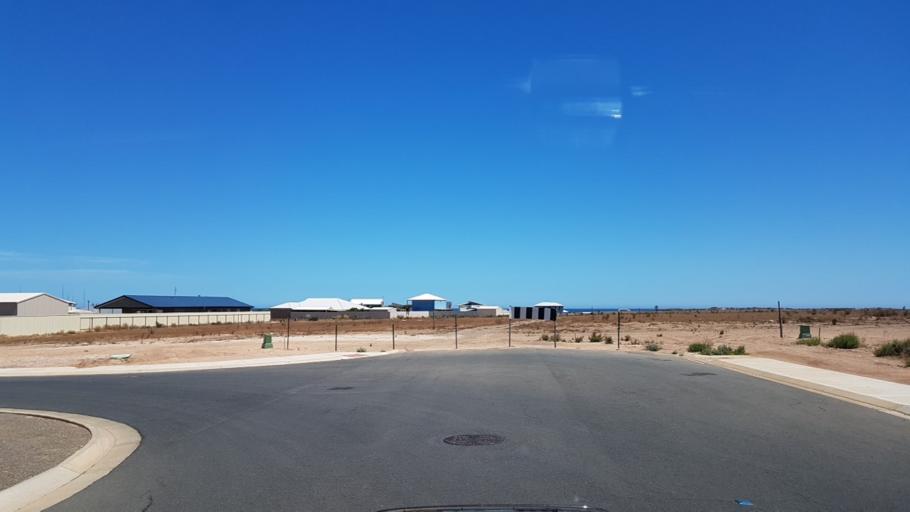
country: AU
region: South Australia
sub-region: Copper Coast
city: Wallaroo
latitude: -33.8919
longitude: 137.6310
